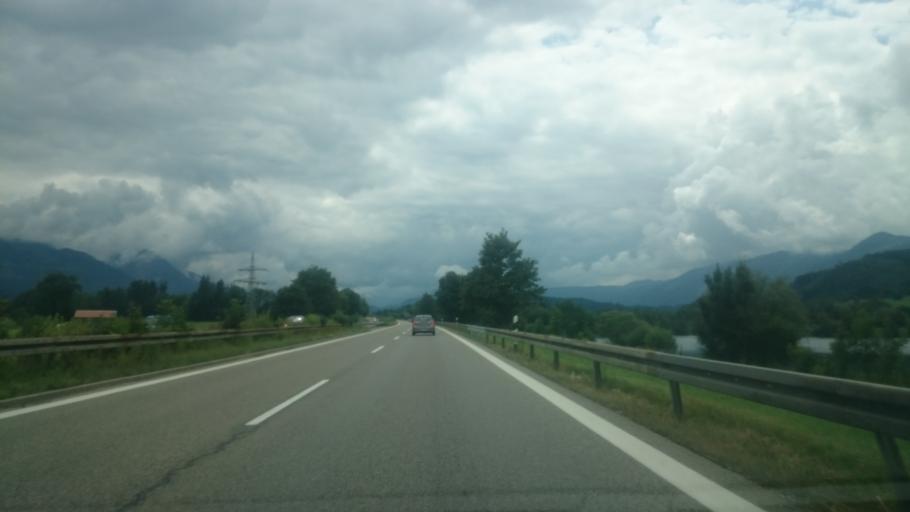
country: DE
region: Bavaria
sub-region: Swabia
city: Blaichach
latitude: 47.5361
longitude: 10.2668
